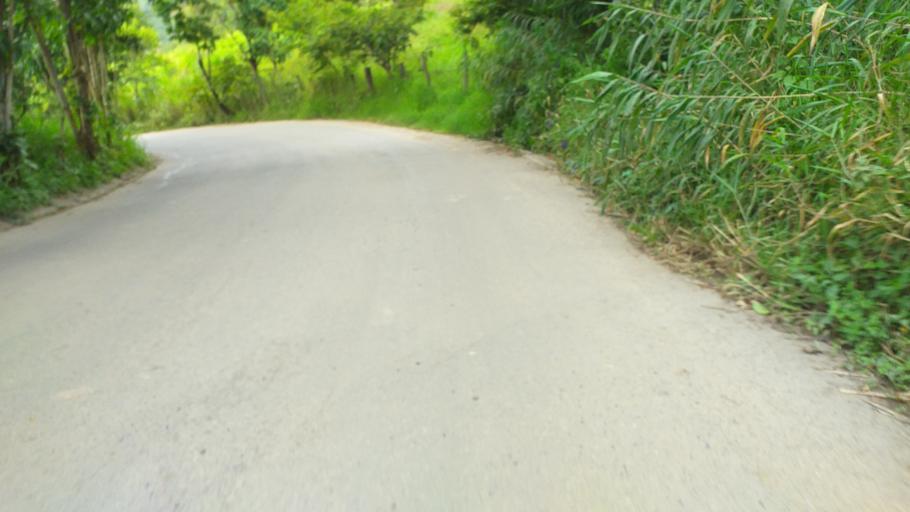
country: CO
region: Cundinamarca
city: Tenza
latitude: 5.0909
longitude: -73.4433
